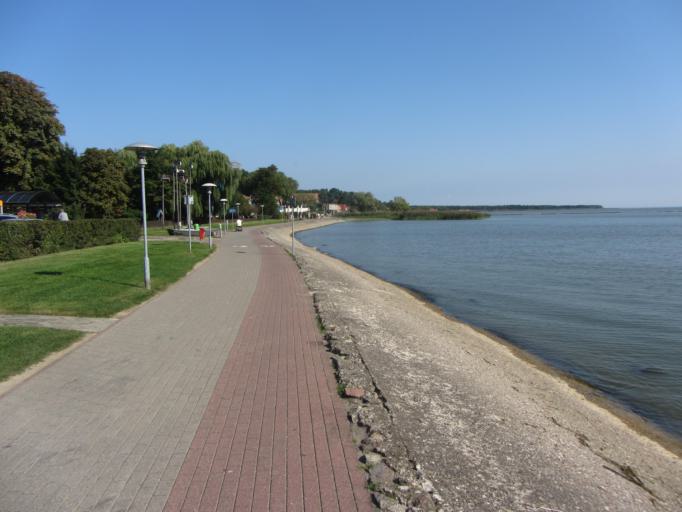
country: LT
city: Nida
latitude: 55.3069
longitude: 21.0079
